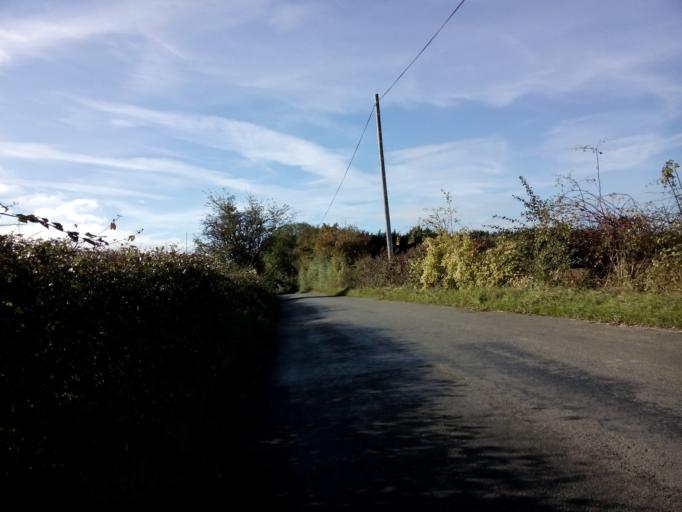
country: GB
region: England
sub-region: Suffolk
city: Capel Saint Mary
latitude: 52.0353
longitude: 1.0218
